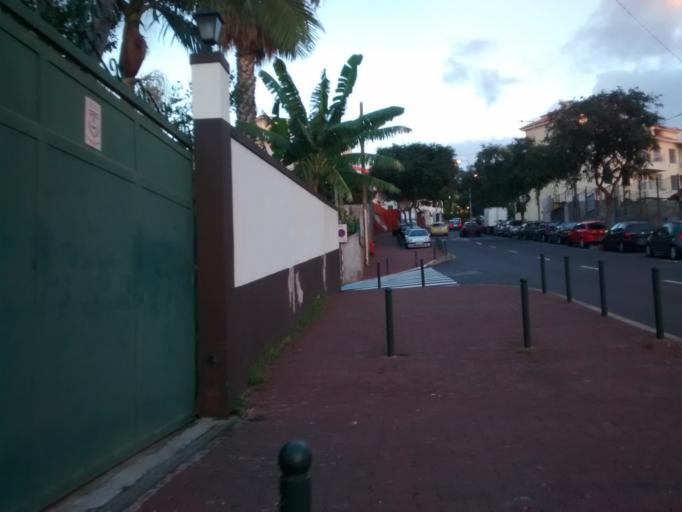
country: PT
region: Madeira
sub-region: Funchal
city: Nossa Senhora do Monte
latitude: 32.6502
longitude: -16.8994
